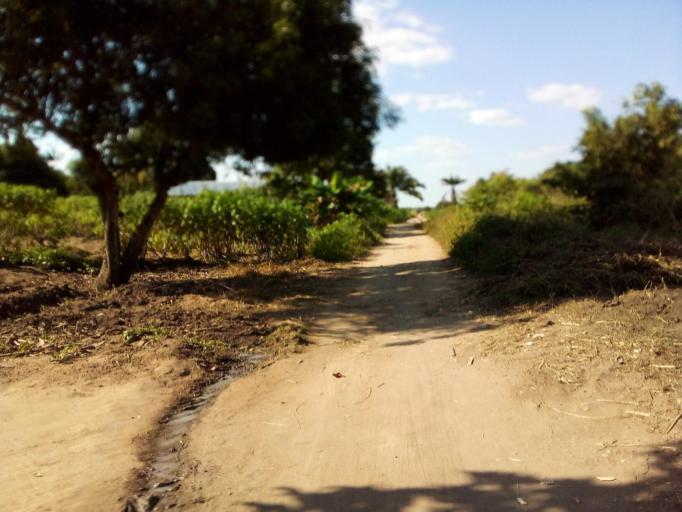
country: MZ
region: Zambezia
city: Quelimane
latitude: -17.5923
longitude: 36.8336
